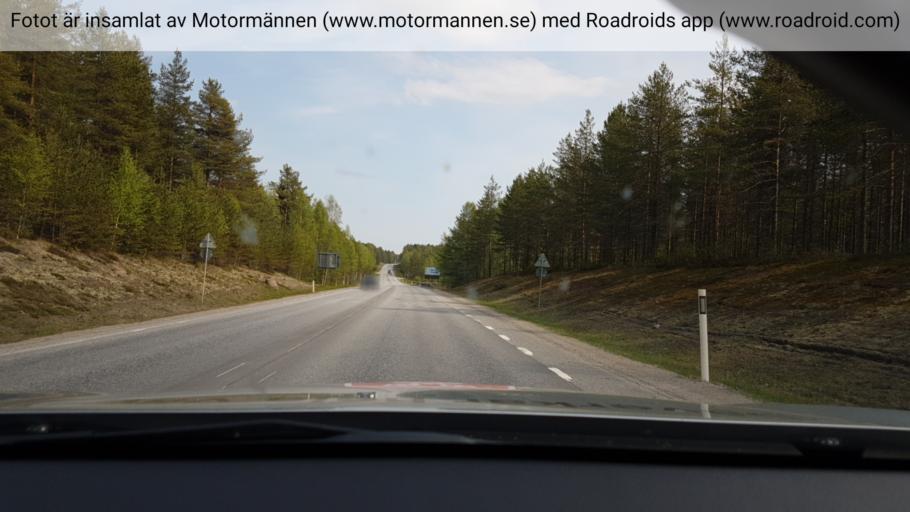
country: SE
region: Vaesterbotten
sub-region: Umea Kommun
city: Roback
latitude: 63.8452
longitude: 20.1634
